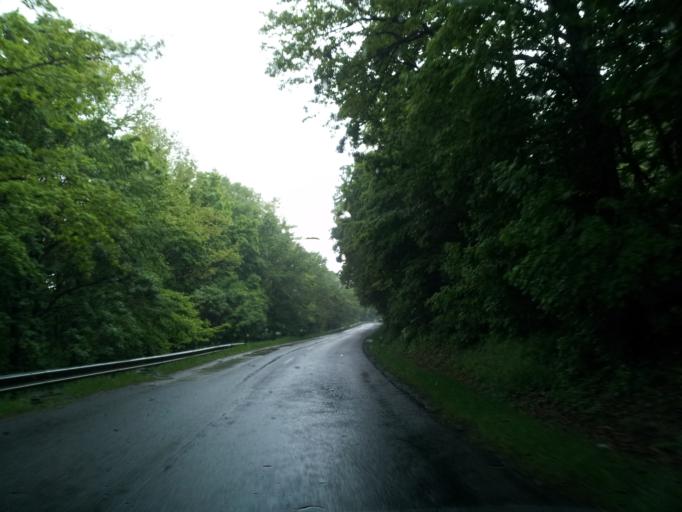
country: HU
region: Baranya
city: Hosszuheteny
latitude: 46.1771
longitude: 18.3216
